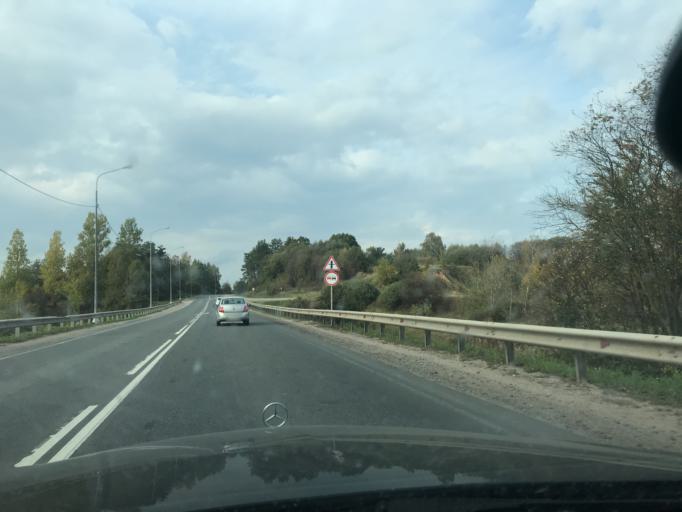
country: RU
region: Pskov
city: Ostrov
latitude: 57.3018
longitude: 28.3725
